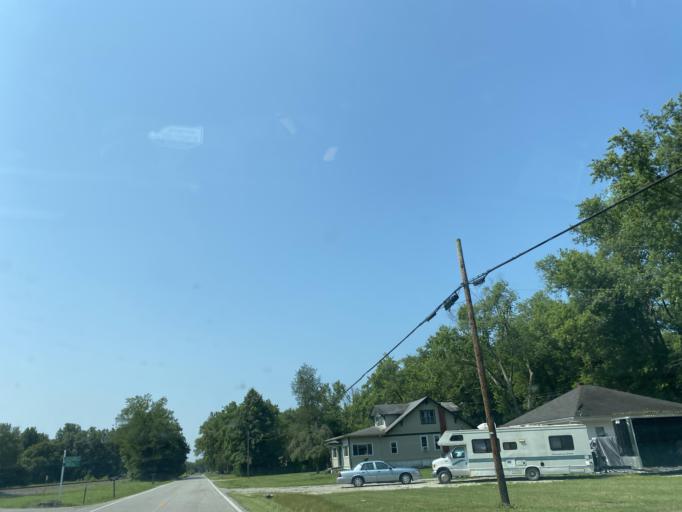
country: US
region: Kentucky
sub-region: Campbell County
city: Claryville
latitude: 38.8784
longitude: -84.4507
